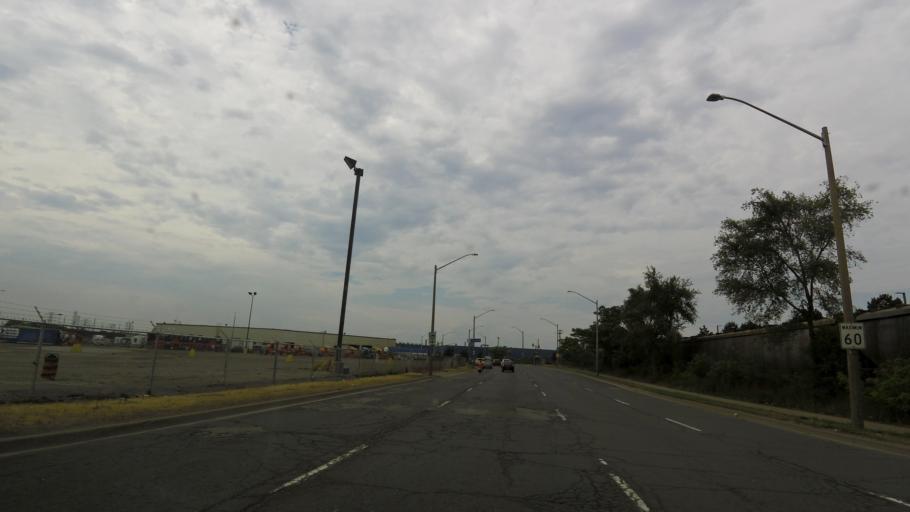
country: CA
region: Ontario
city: Hamilton
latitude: 43.2613
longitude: -79.8104
